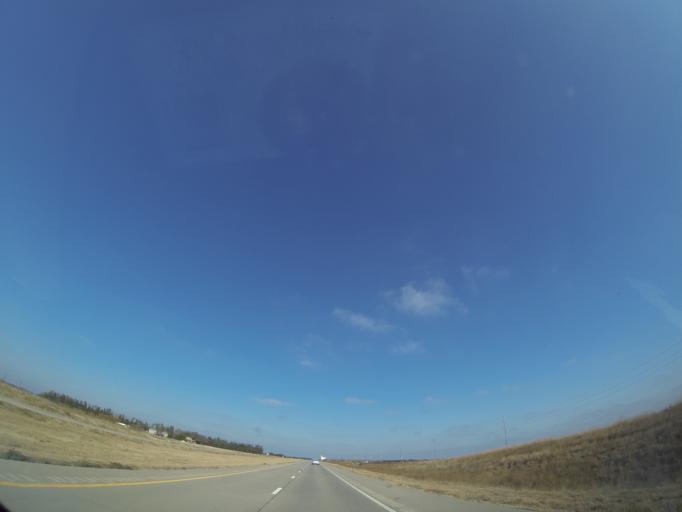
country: US
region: Kansas
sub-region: McPherson County
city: Inman
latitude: 38.2074
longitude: -97.7968
